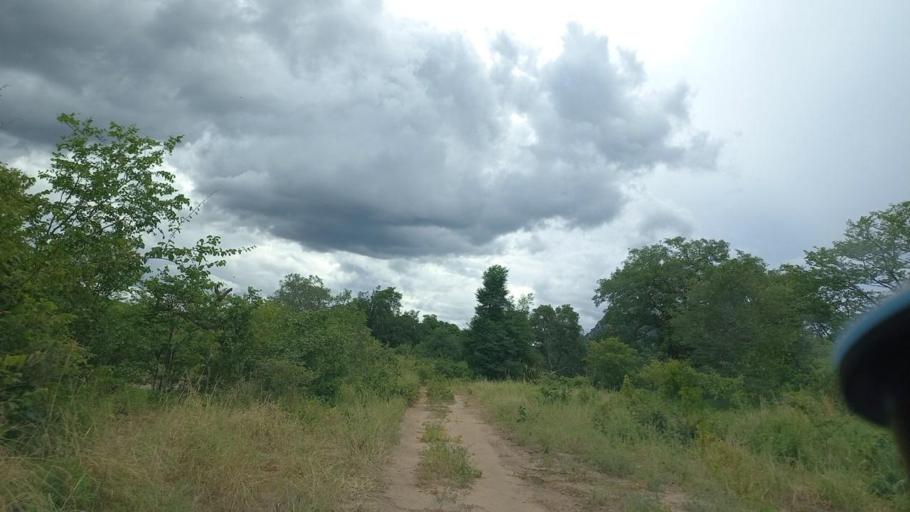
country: ZM
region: Lusaka
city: Luangwa
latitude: -15.6156
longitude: 30.2771
